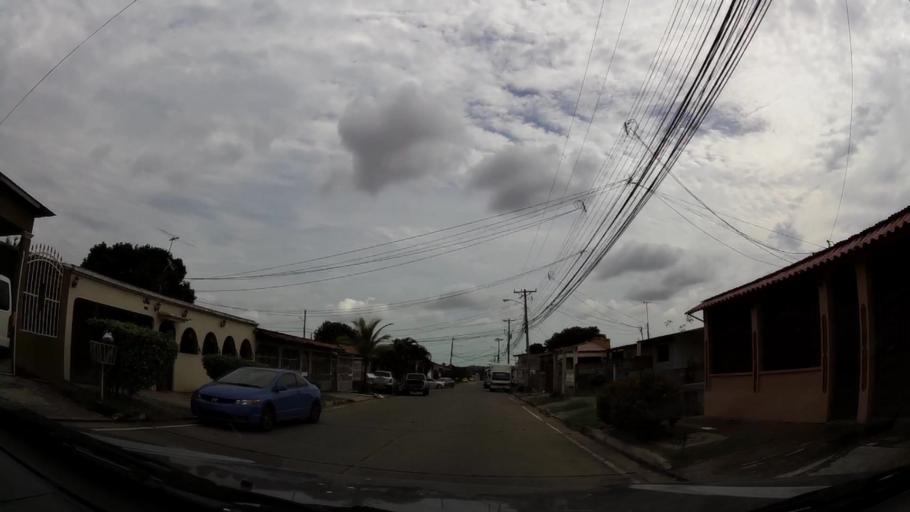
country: PA
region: Panama
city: San Miguelito
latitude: 9.0523
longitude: -79.4191
